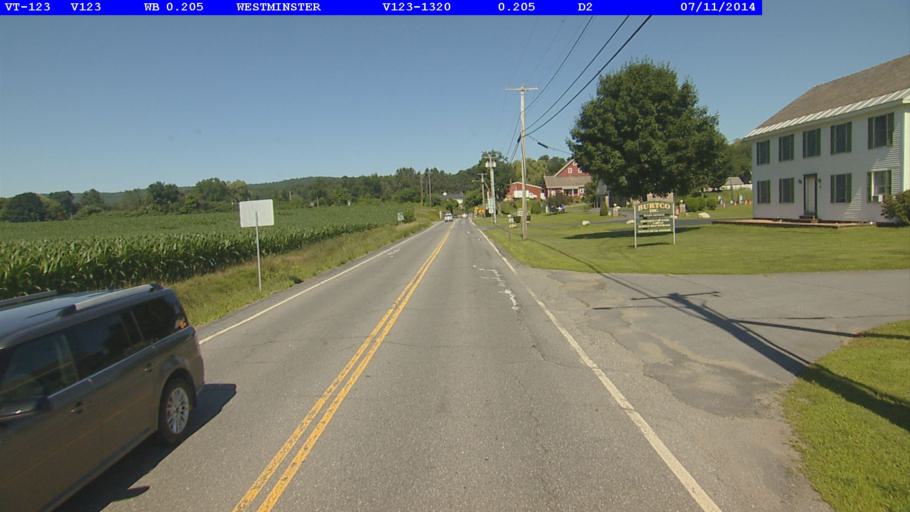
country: US
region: Vermont
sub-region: Windham County
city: Bellows Falls
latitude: 43.0848
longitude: -72.4361
